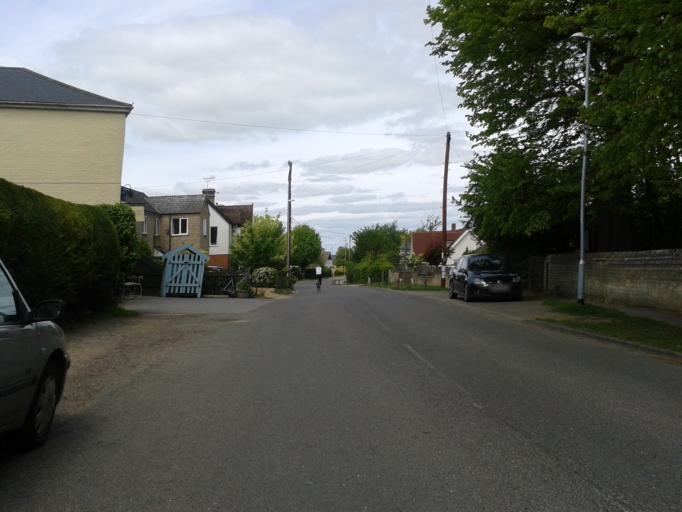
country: GB
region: England
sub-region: Cambridgeshire
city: Haslingfield
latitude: 52.1495
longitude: 0.0498
